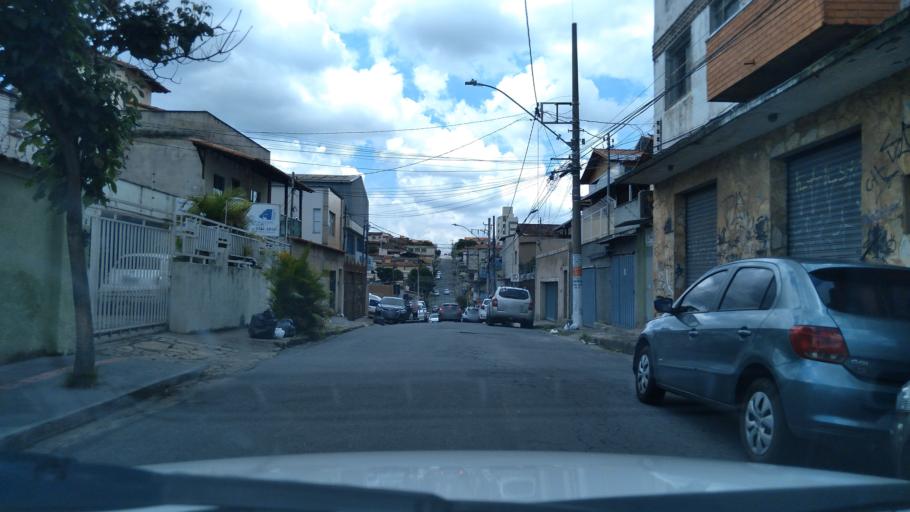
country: BR
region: Minas Gerais
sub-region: Belo Horizonte
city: Belo Horizonte
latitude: -19.9194
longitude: -43.9089
